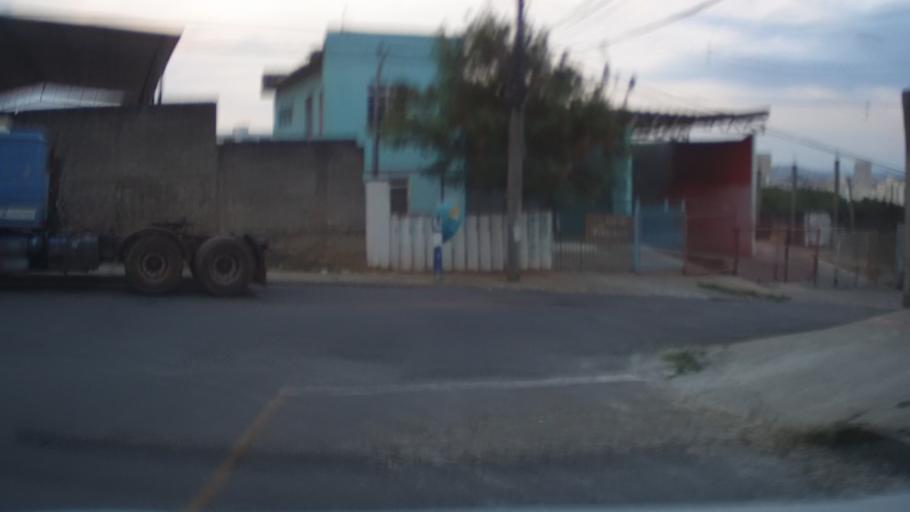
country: BR
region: Minas Gerais
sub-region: Belo Horizonte
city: Belo Horizonte
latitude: -19.8871
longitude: -43.9328
